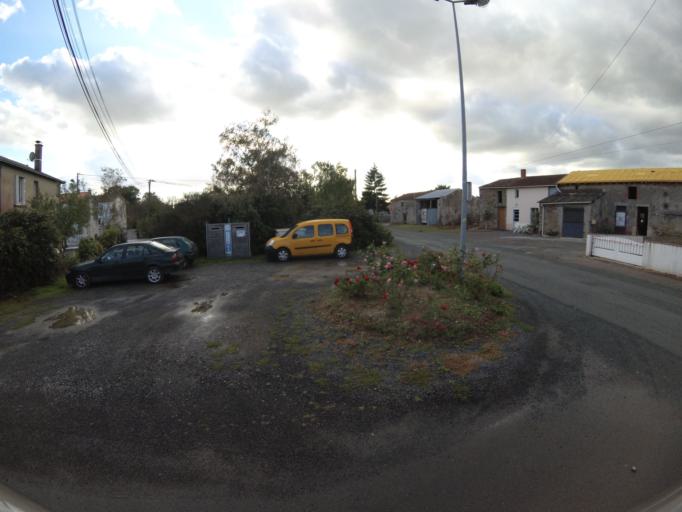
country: FR
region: Pays de la Loire
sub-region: Departement de la Loire-Atlantique
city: Saint-Lumine-de-Clisson
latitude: 47.0821
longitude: -1.3463
